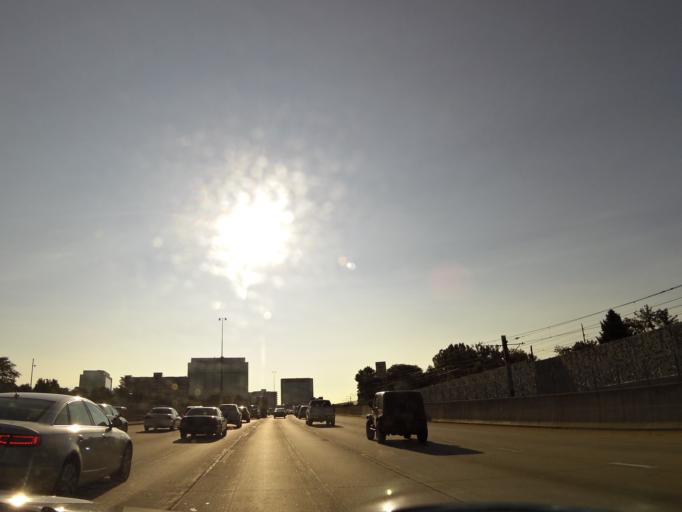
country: US
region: Colorado
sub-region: Arapahoe County
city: Glendale
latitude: 39.6845
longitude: -104.9481
